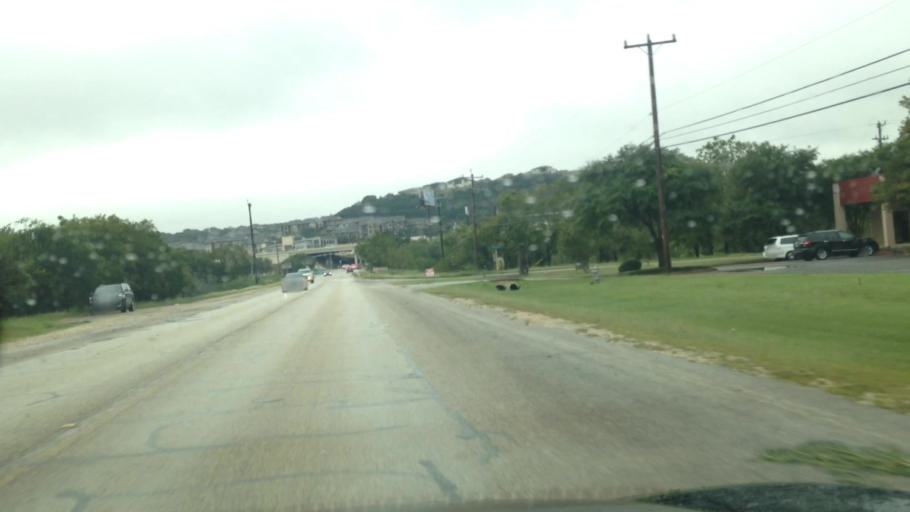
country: US
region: Texas
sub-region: Bexar County
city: Cross Mountain
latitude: 29.6275
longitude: -98.6063
